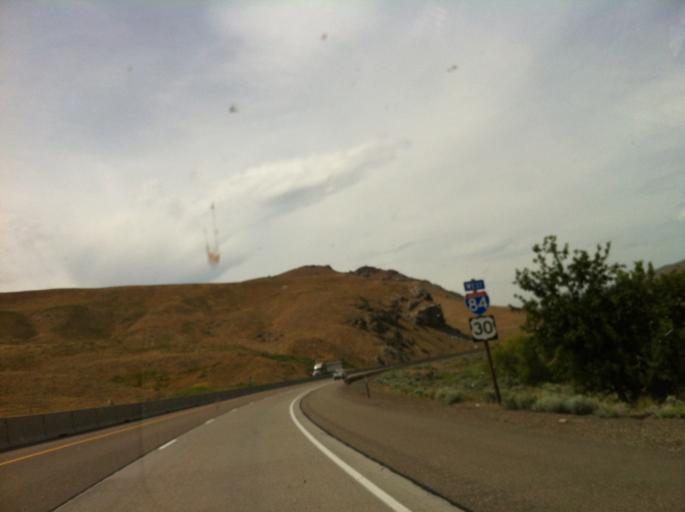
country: US
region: Idaho
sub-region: Washington County
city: Weiser
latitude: 44.3675
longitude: -117.2953
